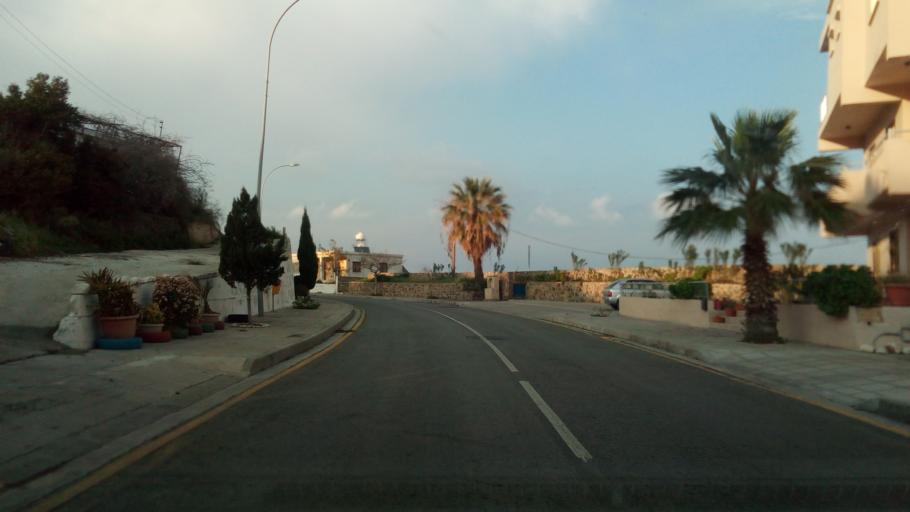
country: CY
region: Lefkosia
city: Kato Pyrgos
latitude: 35.1904
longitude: 32.6701
